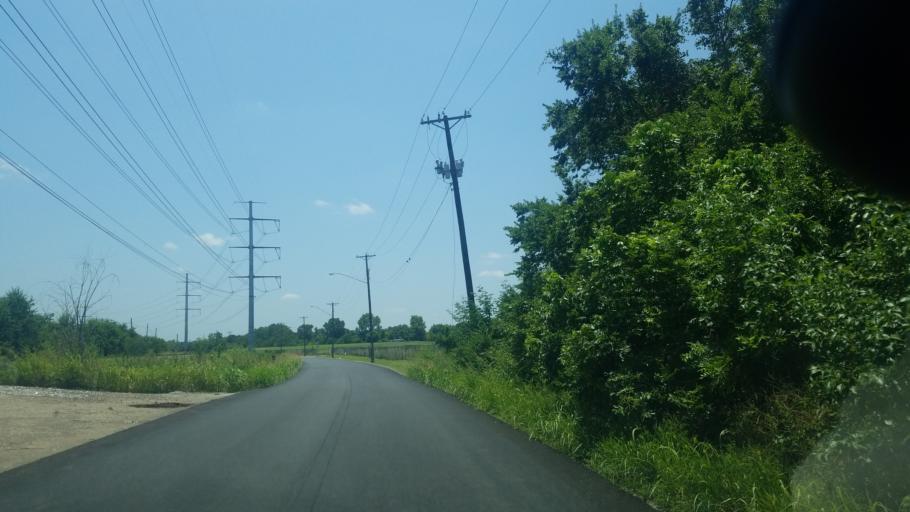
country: US
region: Texas
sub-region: Dallas County
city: Dallas
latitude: 32.7418
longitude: -96.7813
